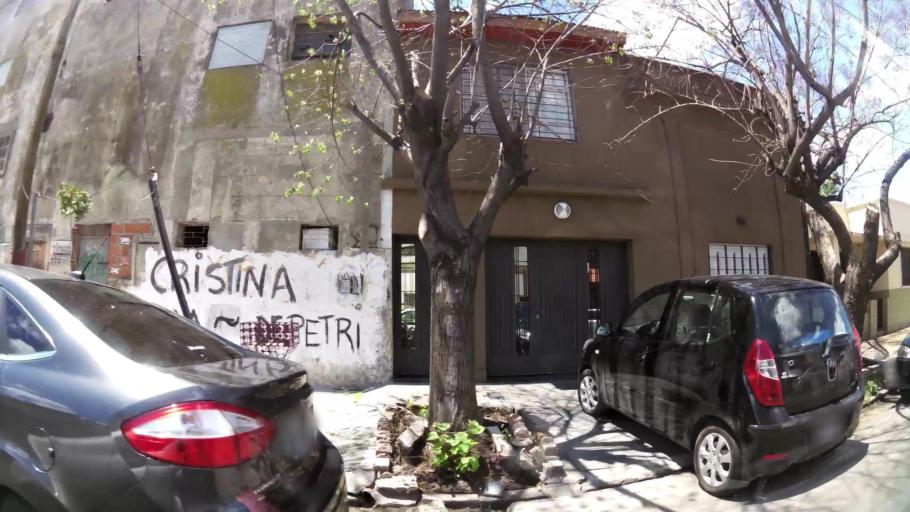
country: AR
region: Buenos Aires
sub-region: Partido de Lanus
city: Lanus
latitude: -34.7287
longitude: -58.3978
